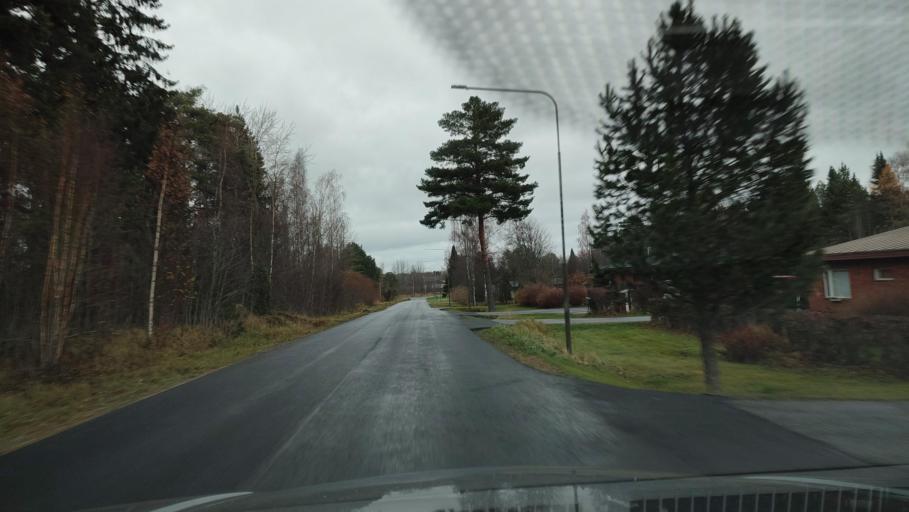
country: FI
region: Ostrobothnia
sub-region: Sydosterbotten
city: Kristinestad
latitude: 62.2741
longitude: 21.3990
